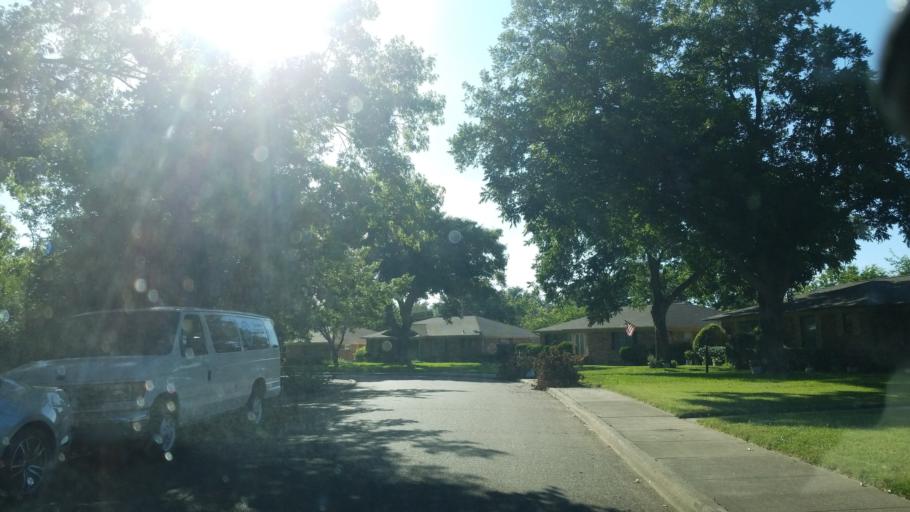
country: US
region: Texas
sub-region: Dallas County
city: Highland Park
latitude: 32.7900
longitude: -96.7080
